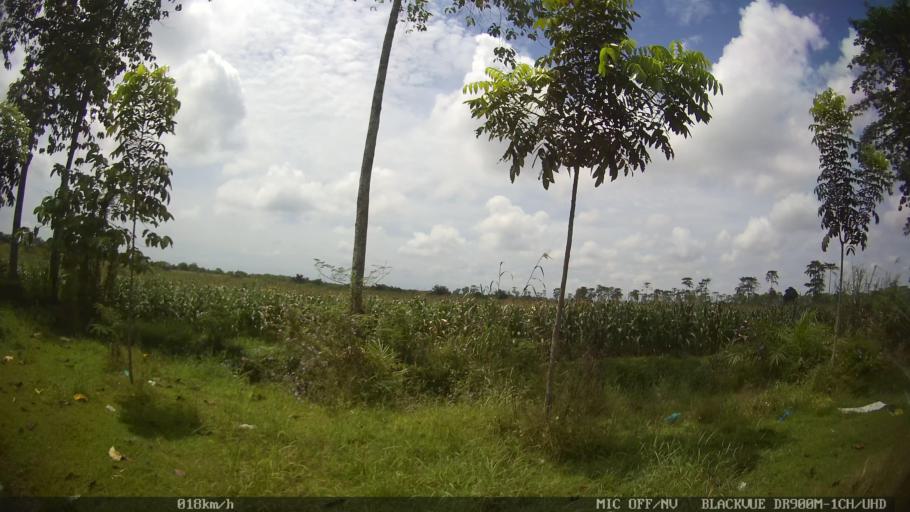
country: ID
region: North Sumatra
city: Percut
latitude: 3.6200
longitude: 98.7709
